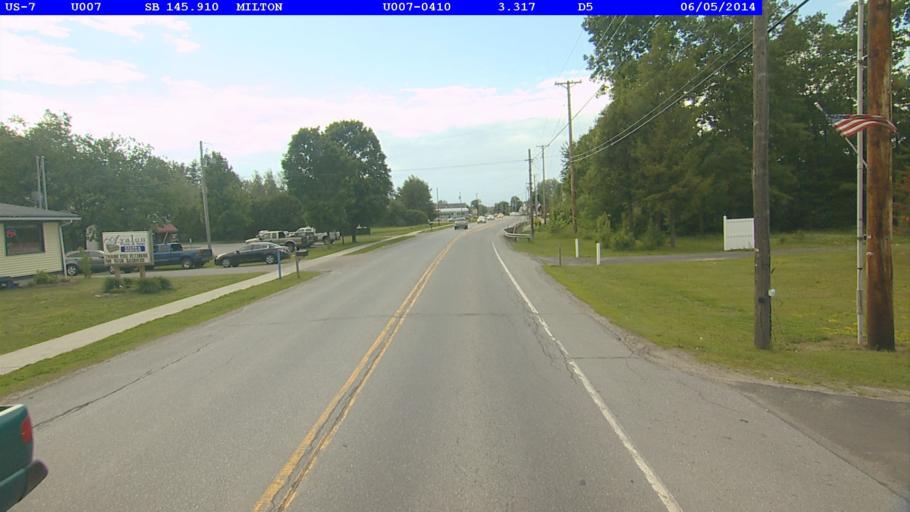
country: US
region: Vermont
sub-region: Chittenden County
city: Milton
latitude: 44.6220
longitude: -73.1291
